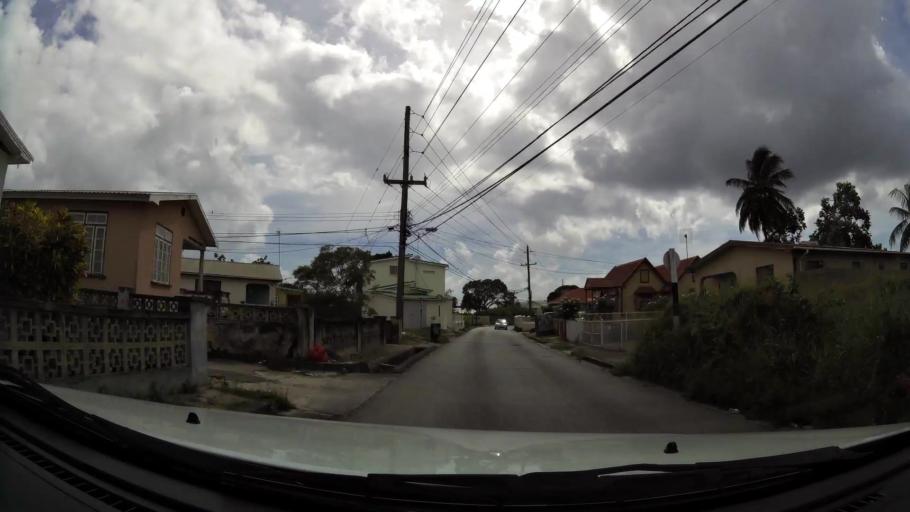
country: BB
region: Saint Michael
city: Bridgetown
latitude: 13.1136
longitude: -59.6248
